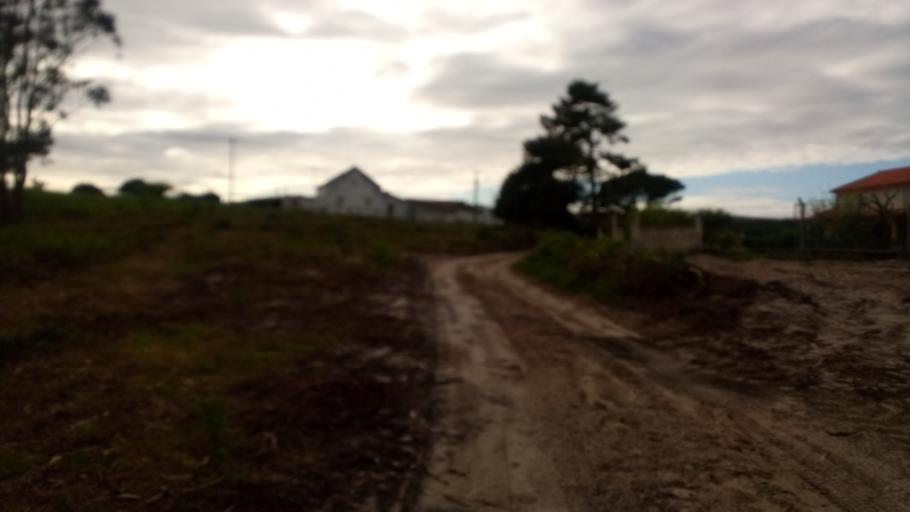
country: PT
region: Leiria
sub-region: Caldas da Rainha
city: Caldas da Rainha
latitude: 39.4522
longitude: -9.1705
